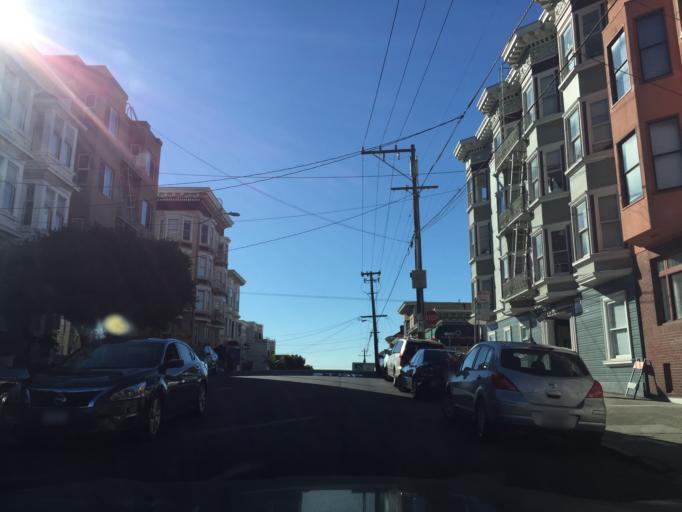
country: US
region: California
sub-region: San Francisco County
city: San Francisco
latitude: 37.7934
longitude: -122.4162
